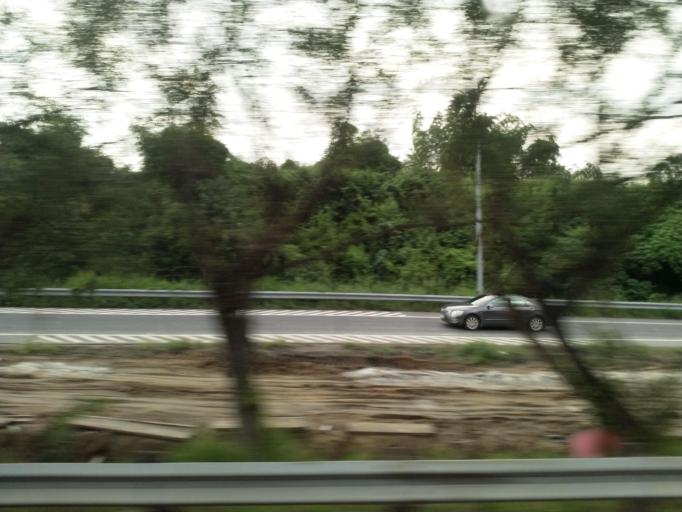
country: TW
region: Taiwan
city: Fengshan
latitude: 22.7553
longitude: 120.3694
